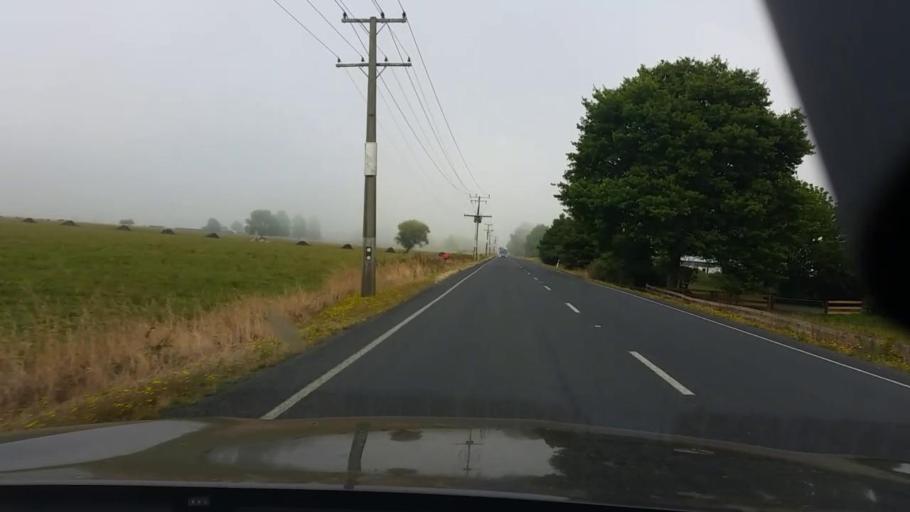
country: NZ
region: Waikato
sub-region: Hamilton City
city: Hamilton
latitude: -37.6281
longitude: 175.3178
